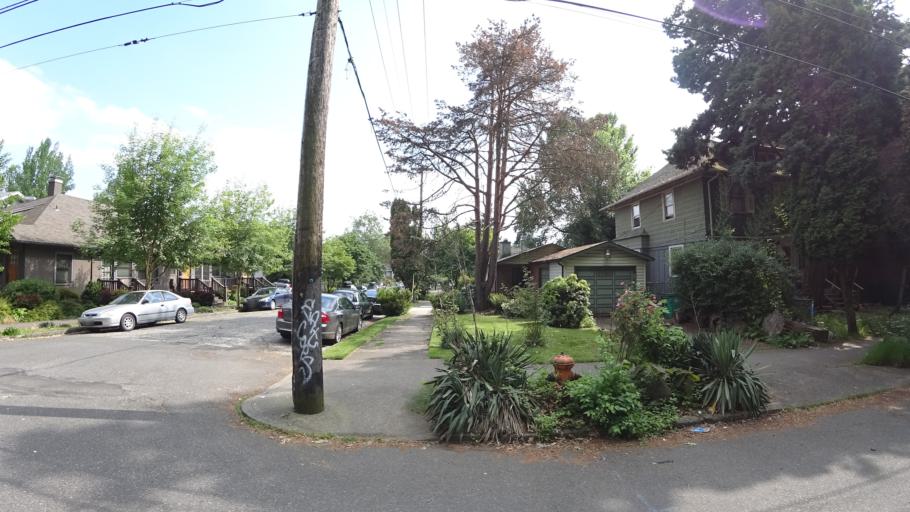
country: US
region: Oregon
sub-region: Multnomah County
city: Portland
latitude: 45.5193
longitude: -122.6246
